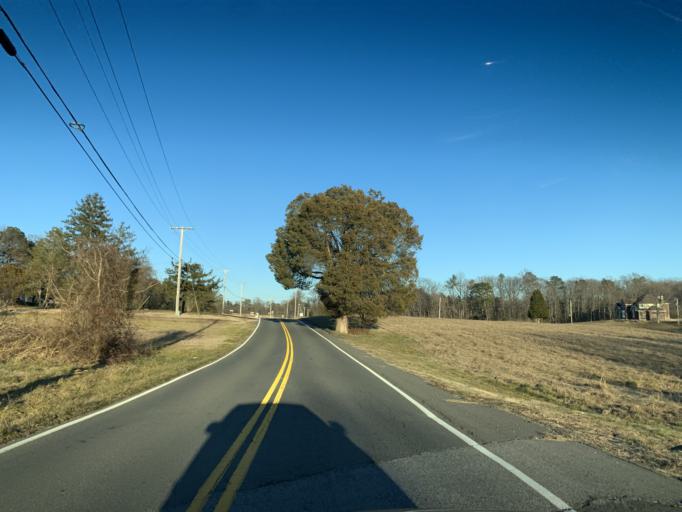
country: US
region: Maryland
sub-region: Saint Mary's County
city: Mechanicsville
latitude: 38.4453
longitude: -76.7267
